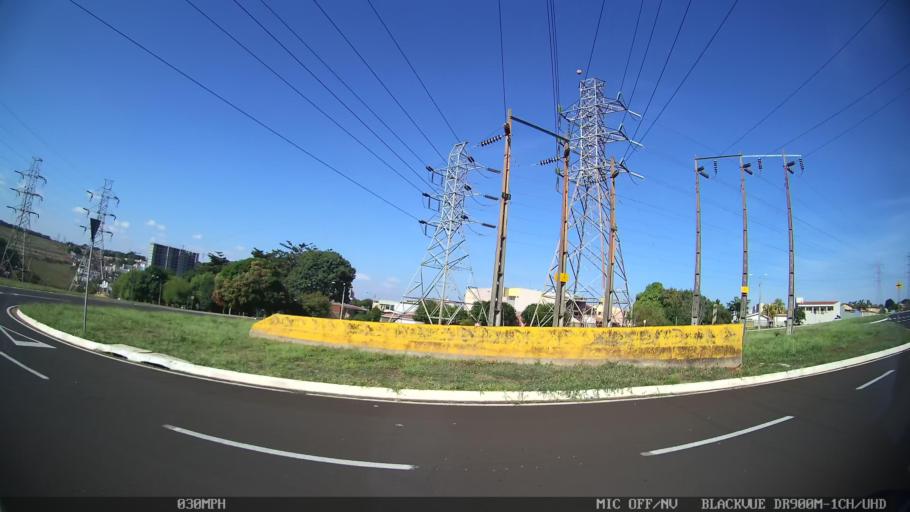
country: BR
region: Sao Paulo
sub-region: Ribeirao Preto
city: Ribeirao Preto
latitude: -21.1793
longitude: -47.7829
